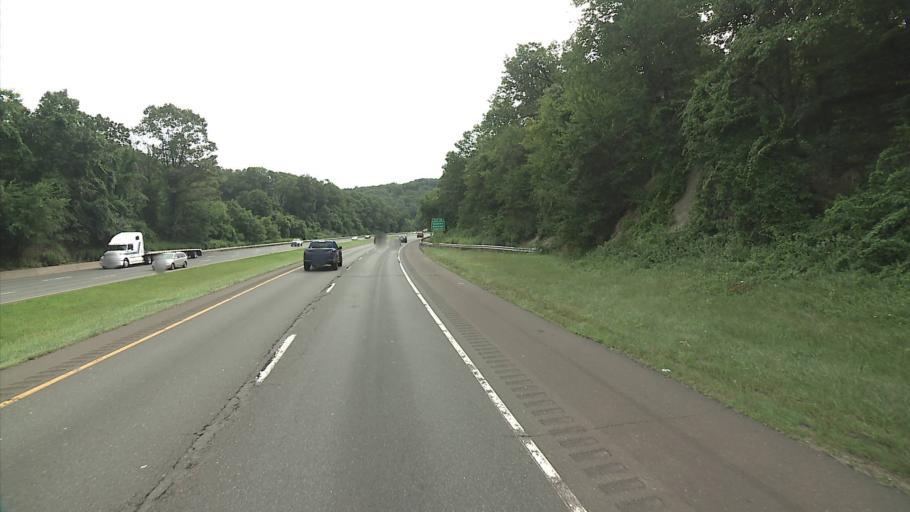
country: US
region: Connecticut
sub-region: Fairfield County
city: Newtown
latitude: 41.4285
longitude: -73.3197
